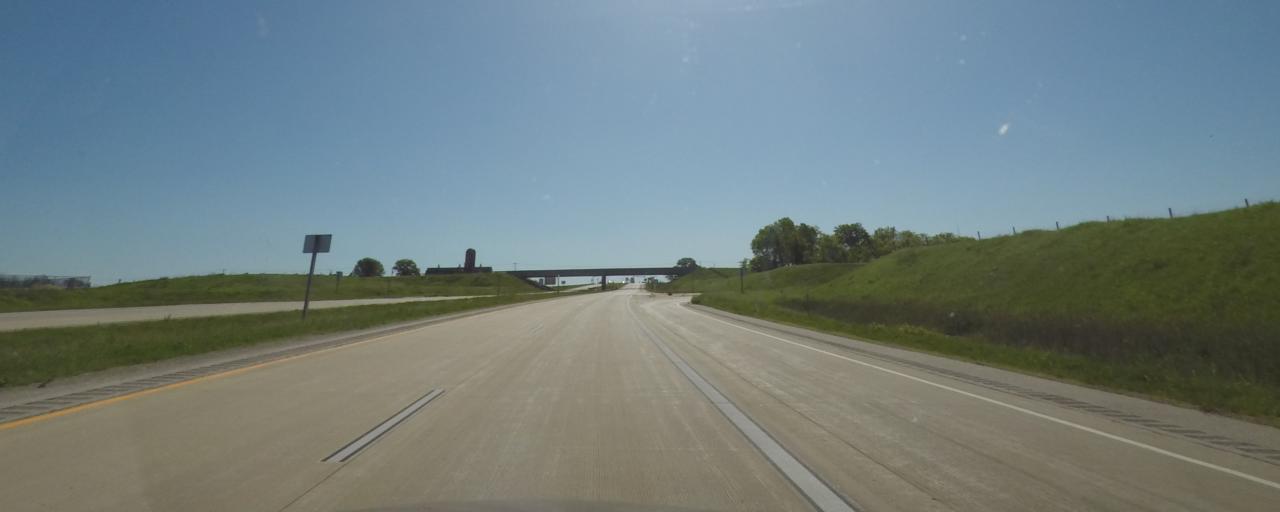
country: US
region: Wisconsin
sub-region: Fond du Lac County
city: Fond du Lac
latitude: 43.7373
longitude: -88.4537
